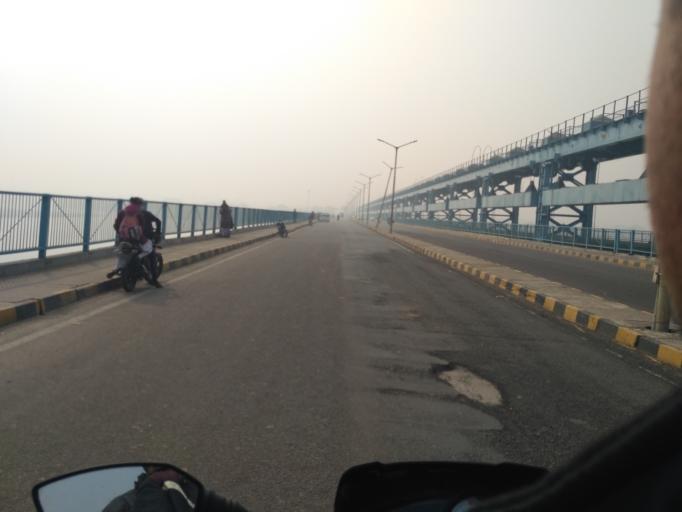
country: IN
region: Uttar Pradesh
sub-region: Kanpur
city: Nawabganj
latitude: 26.5122
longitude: 80.3204
